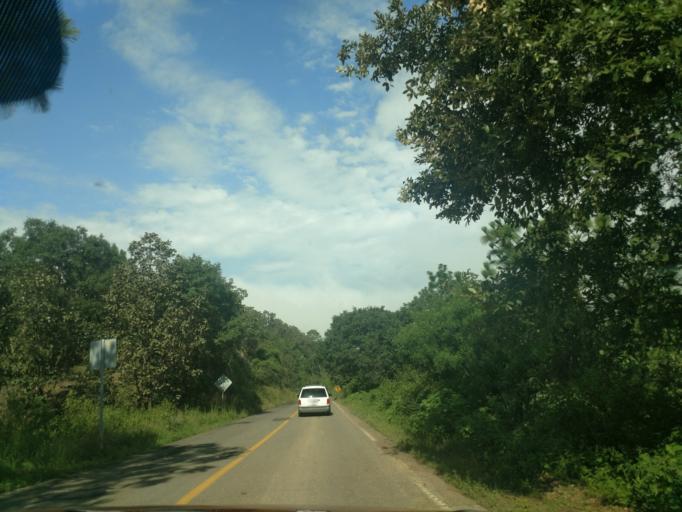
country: MX
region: Jalisco
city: El Salto
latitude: 20.4619
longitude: -104.3810
